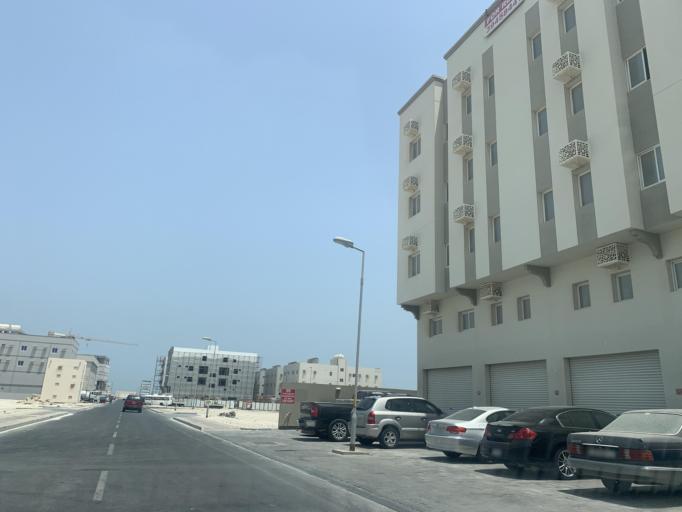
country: BH
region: Muharraq
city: Al Hadd
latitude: 26.2606
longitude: 50.6683
